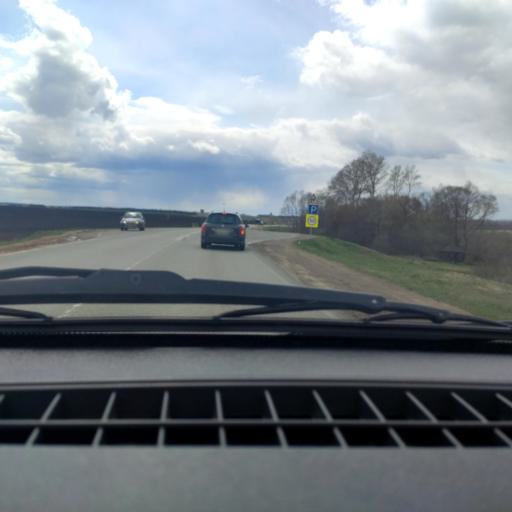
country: RU
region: Bashkortostan
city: Kushnarenkovo
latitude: 55.0681
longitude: 55.2579
